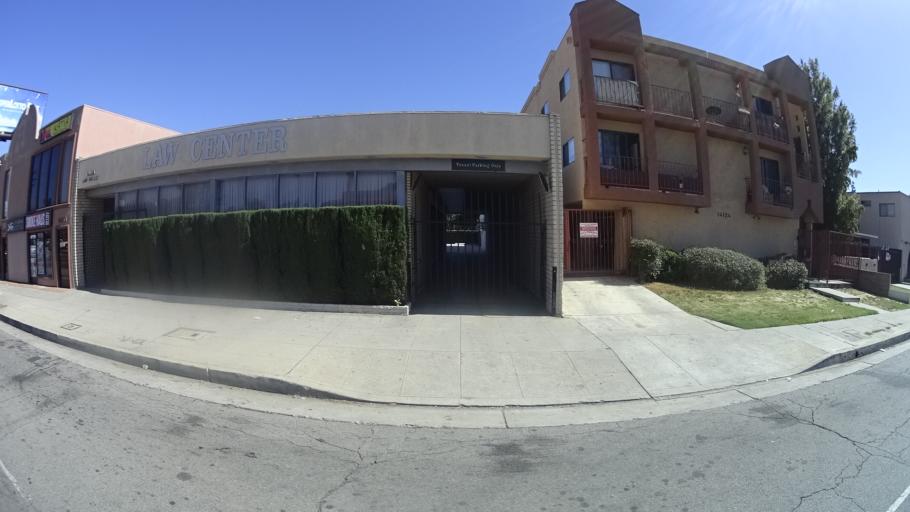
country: US
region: California
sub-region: Los Angeles County
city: Van Nuys
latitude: 34.1867
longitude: -118.4407
